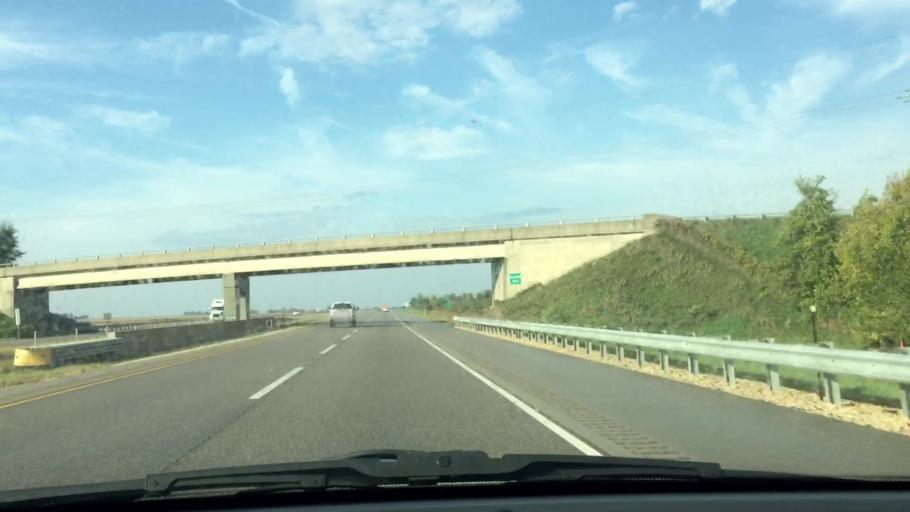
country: US
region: Illinois
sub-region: Ogle County
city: Rochelle
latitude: 41.8759
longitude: -89.1503
